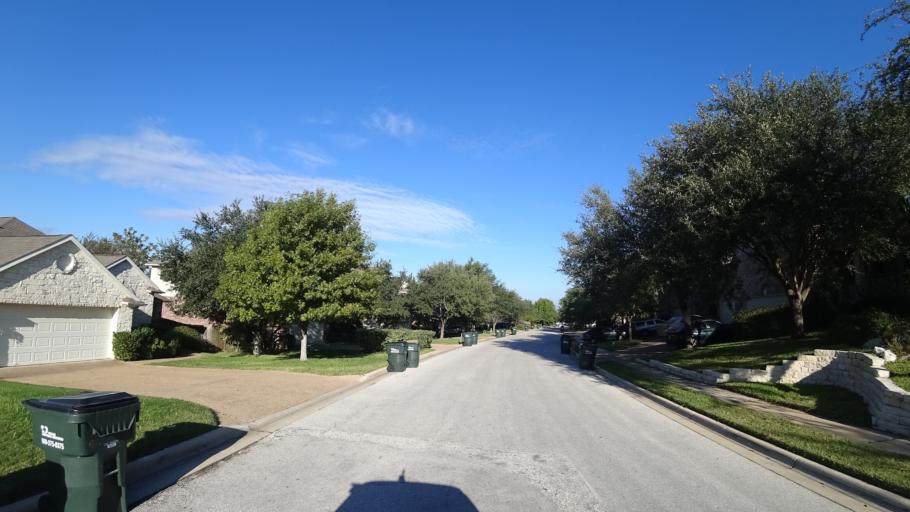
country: US
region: Texas
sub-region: Travis County
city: Hudson Bend
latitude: 30.3694
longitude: -97.9002
